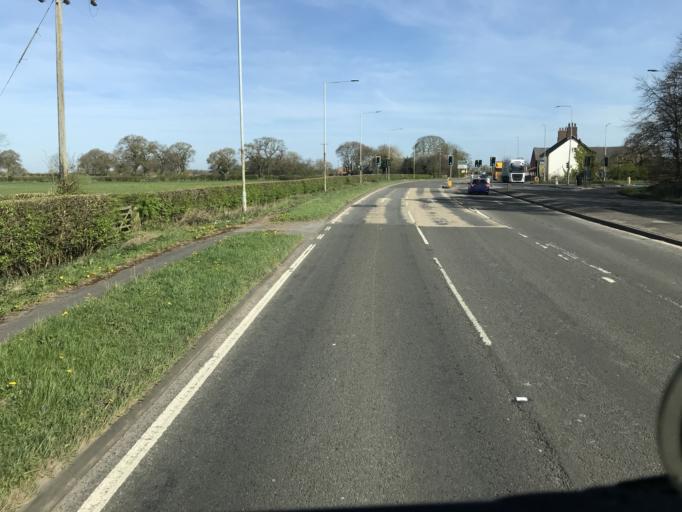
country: GB
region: England
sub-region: Cheshire East
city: Mere
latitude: 53.3006
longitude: -2.4195
